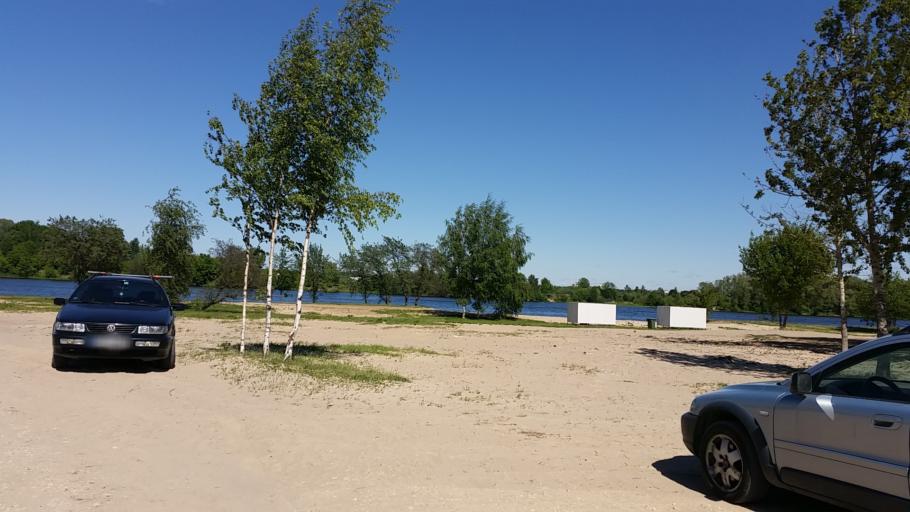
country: LV
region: Riga
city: Riga
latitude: 56.9287
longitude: 24.1181
